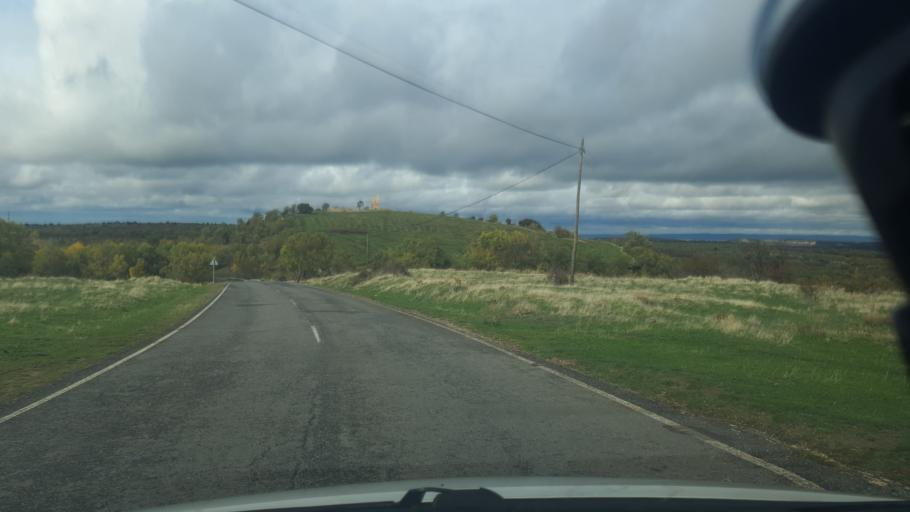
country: ES
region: Castille and Leon
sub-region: Provincia de Segovia
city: Gallegos
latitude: 41.0785
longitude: -3.7867
